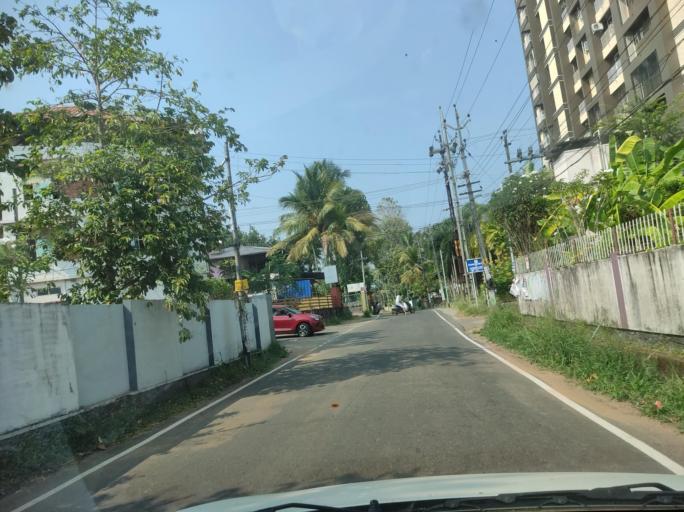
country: IN
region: Kerala
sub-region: Kottayam
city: Kottayam
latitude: 9.5938
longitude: 76.5119
